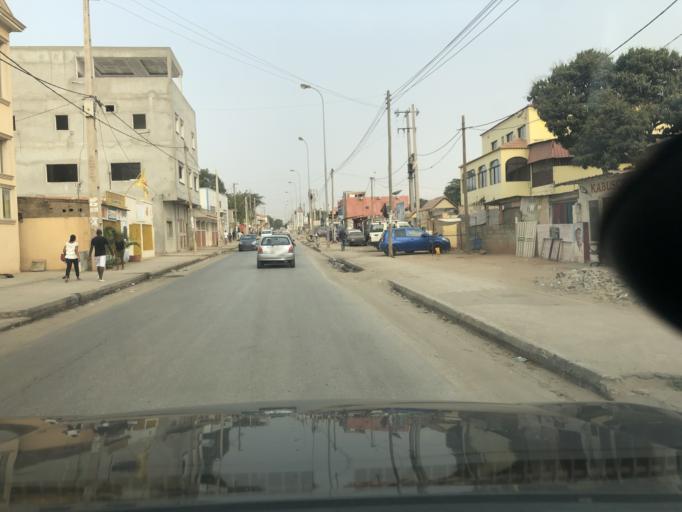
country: AO
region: Luanda
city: Luanda
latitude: -8.8823
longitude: 13.1996
